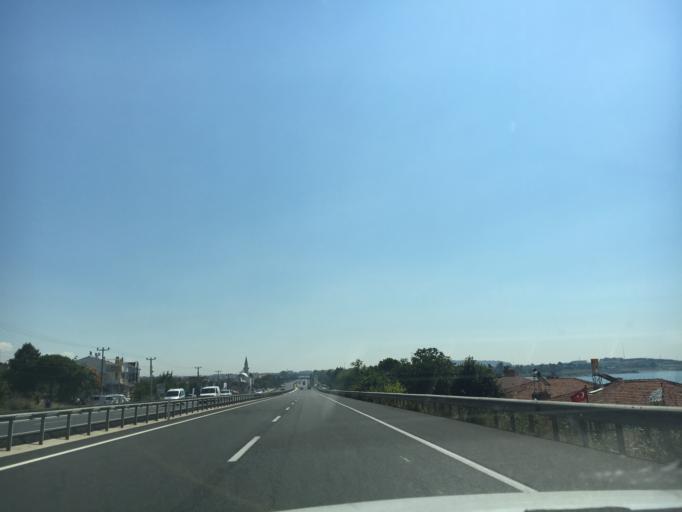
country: TR
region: Tekirdag
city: Marmara Ereglisi
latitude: 40.9708
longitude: 27.9185
